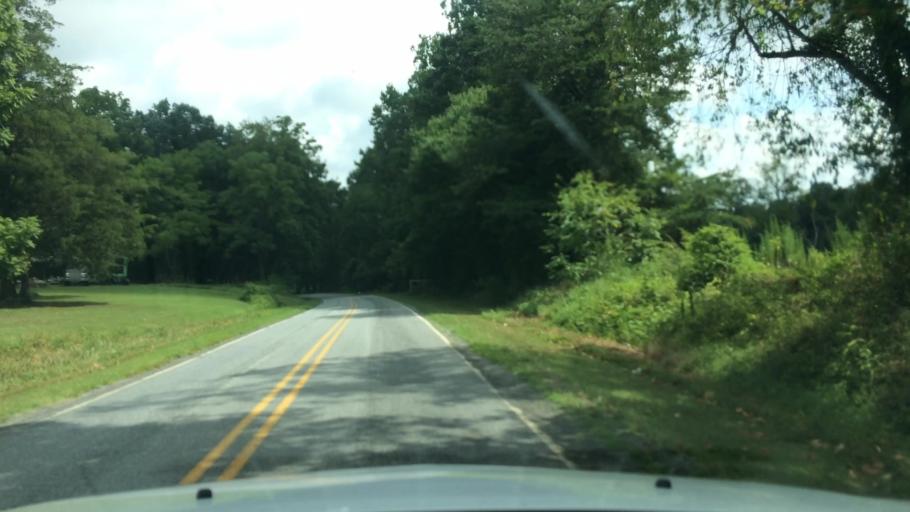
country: US
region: North Carolina
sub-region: Yadkin County
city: Jonesville
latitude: 36.1052
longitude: -80.8585
